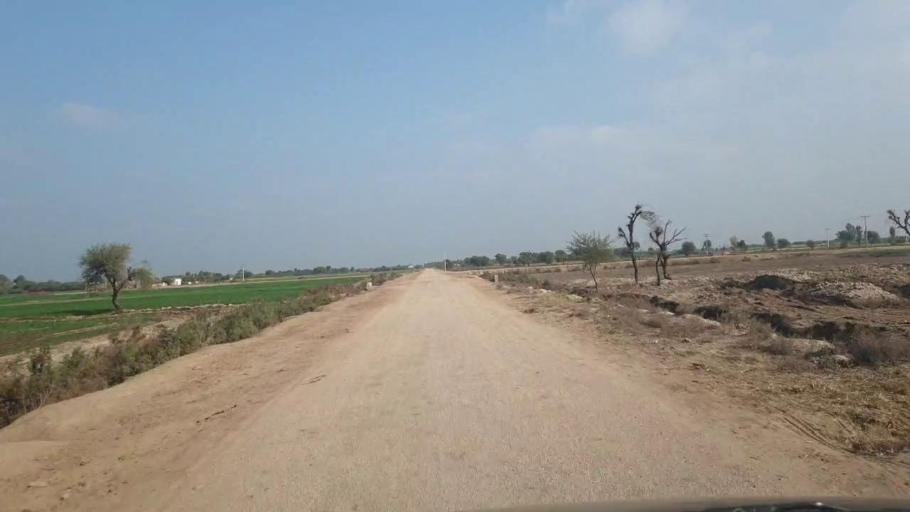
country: PK
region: Sindh
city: Shahdadpur
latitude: 25.9132
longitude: 68.6742
